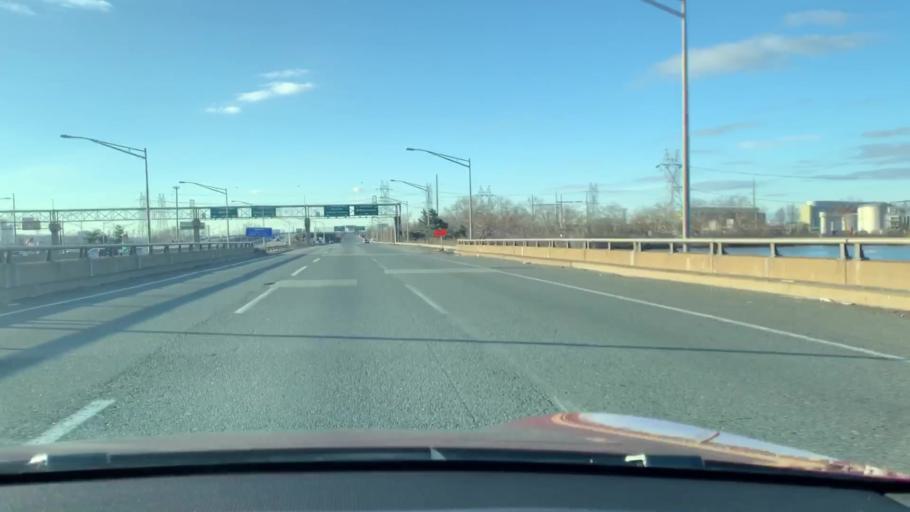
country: US
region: New Jersey
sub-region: Bergen County
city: Ridgefield
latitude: 40.8396
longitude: -74.0190
